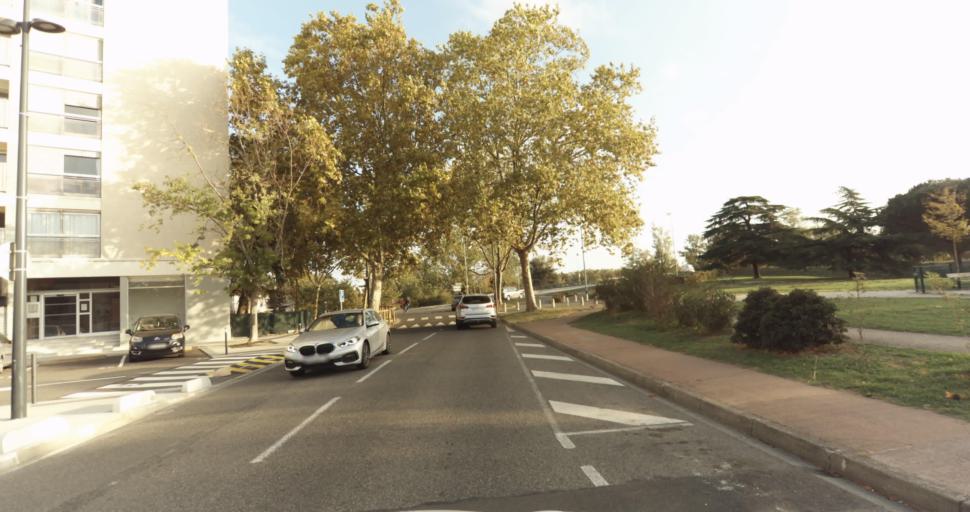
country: FR
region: Midi-Pyrenees
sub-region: Departement de la Haute-Garonne
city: Ramonville-Saint-Agne
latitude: 43.5470
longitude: 1.4786
